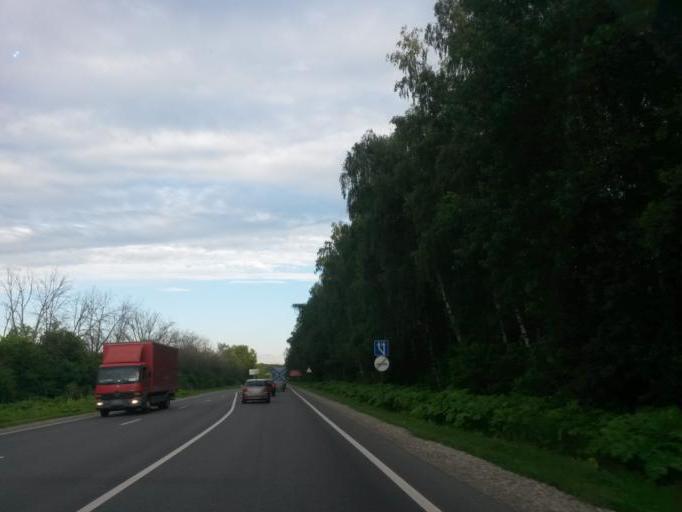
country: RU
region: Moskovskaya
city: Barybino
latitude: 55.2429
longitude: 37.8534
